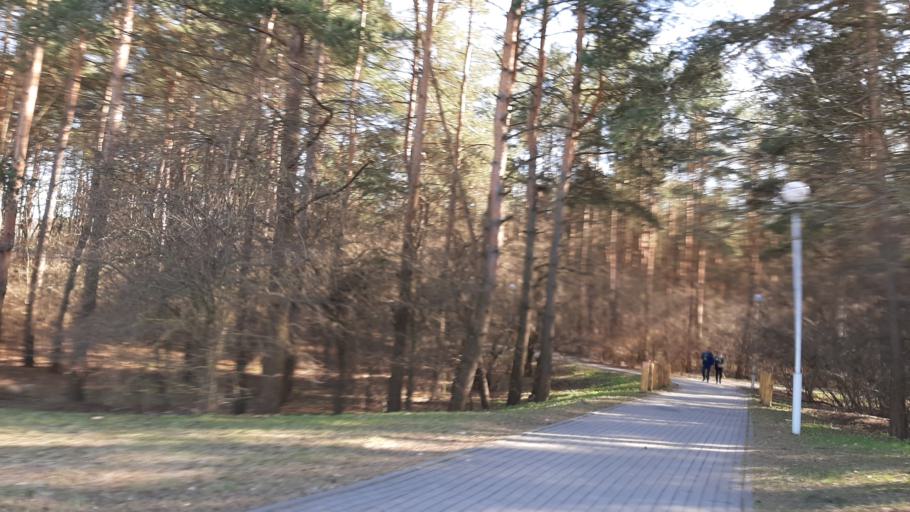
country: BY
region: Minsk
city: Bal'shavik
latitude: 53.9594
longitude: 27.5910
